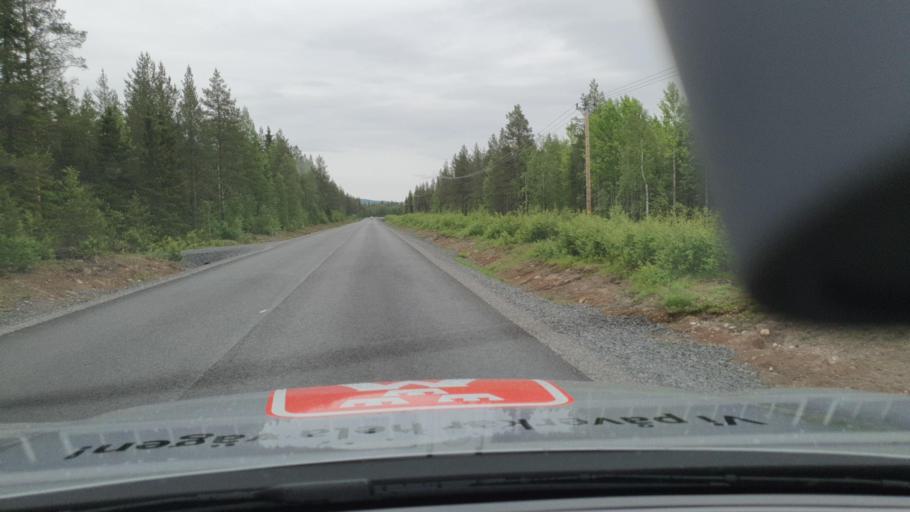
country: SE
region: Norrbotten
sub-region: Overkalix Kommun
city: OEverkalix
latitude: 66.7140
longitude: 23.1963
